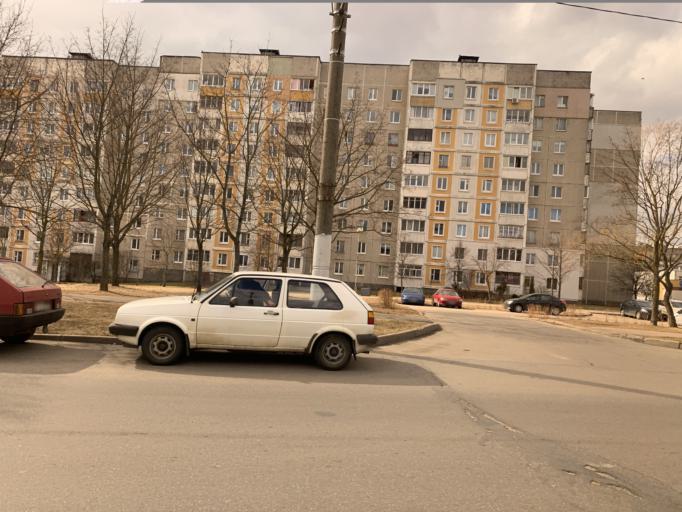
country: BY
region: Minsk
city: Borovlyany
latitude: 53.9350
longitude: 27.6879
